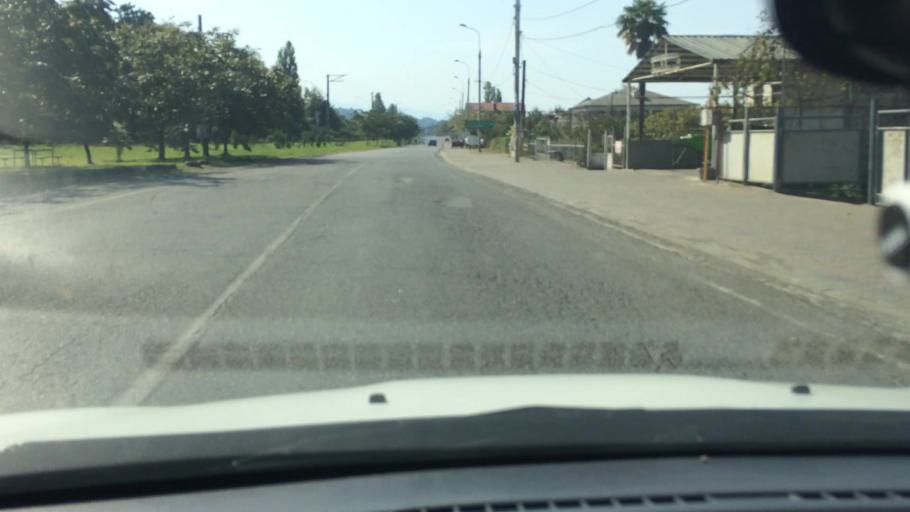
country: GE
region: Ajaria
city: Kobuleti
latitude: 41.8025
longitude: 41.7756
